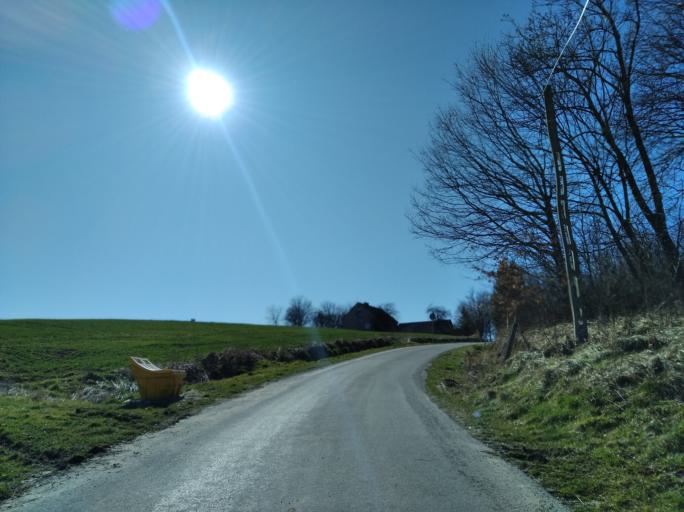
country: PL
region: Subcarpathian Voivodeship
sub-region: Powiat strzyzowski
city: Wisniowa
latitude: 49.9109
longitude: 21.6989
